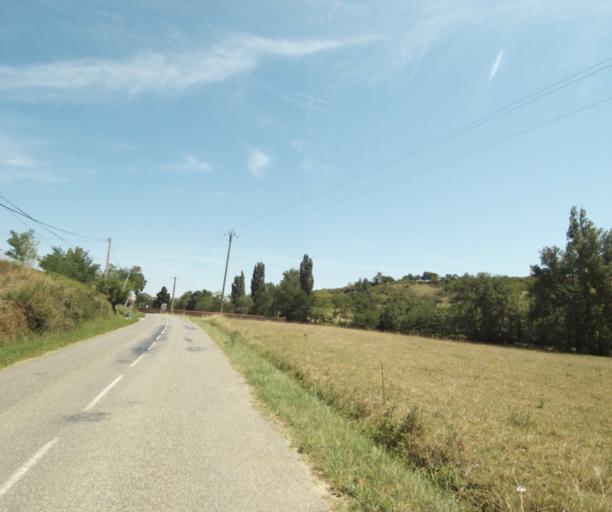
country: FR
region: Midi-Pyrenees
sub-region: Departement de l'Ariege
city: Lezat-sur-Leze
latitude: 43.2730
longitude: 1.3372
